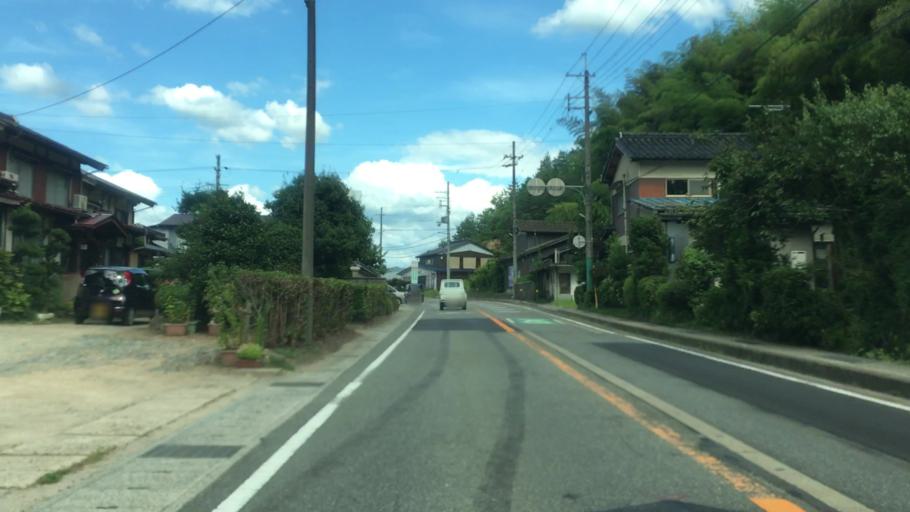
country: JP
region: Hyogo
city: Toyooka
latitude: 35.5536
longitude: 134.8015
